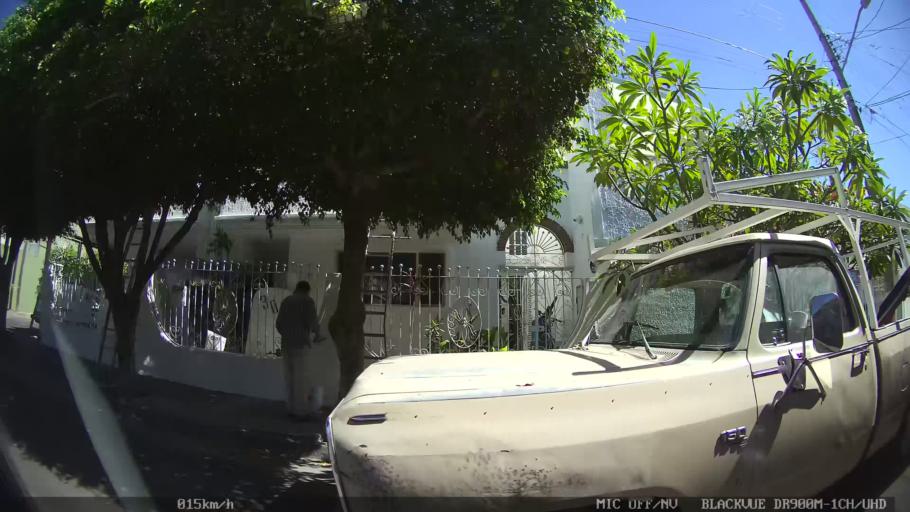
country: MX
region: Jalisco
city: Tlaquepaque
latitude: 20.6469
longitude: -103.2971
